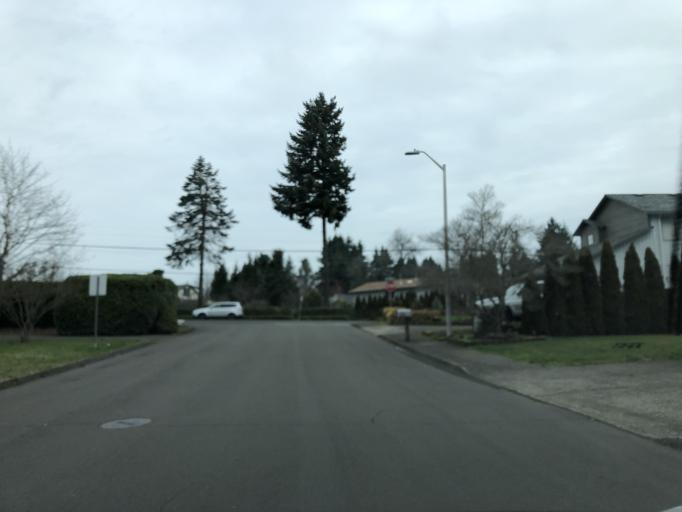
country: US
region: Oregon
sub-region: Washington County
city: Tigard
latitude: 45.4182
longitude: -122.7782
